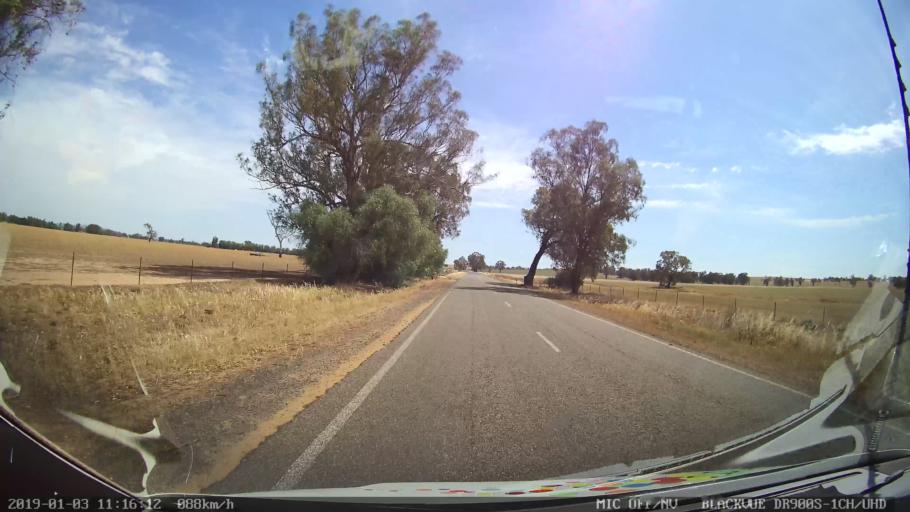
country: AU
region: New South Wales
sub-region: Young
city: Young
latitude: -34.1548
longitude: 148.2693
